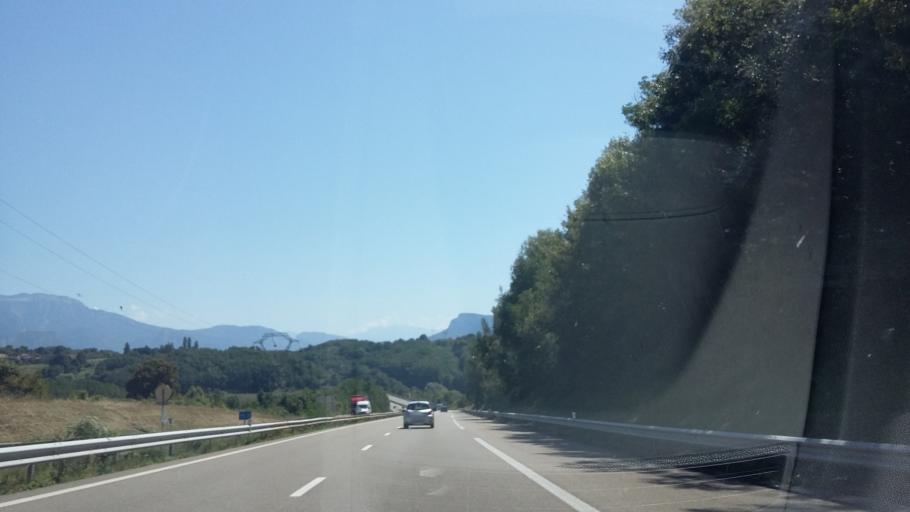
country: FR
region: Rhone-Alpes
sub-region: Departement de l'Isere
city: Rives
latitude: 45.3625
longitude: 5.5134
